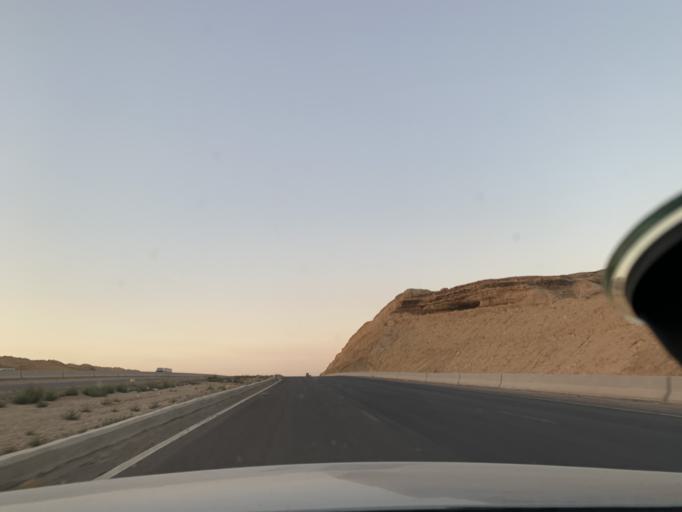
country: EG
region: Muhafazat al Qahirah
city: Halwan
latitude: 29.9492
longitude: 31.5377
